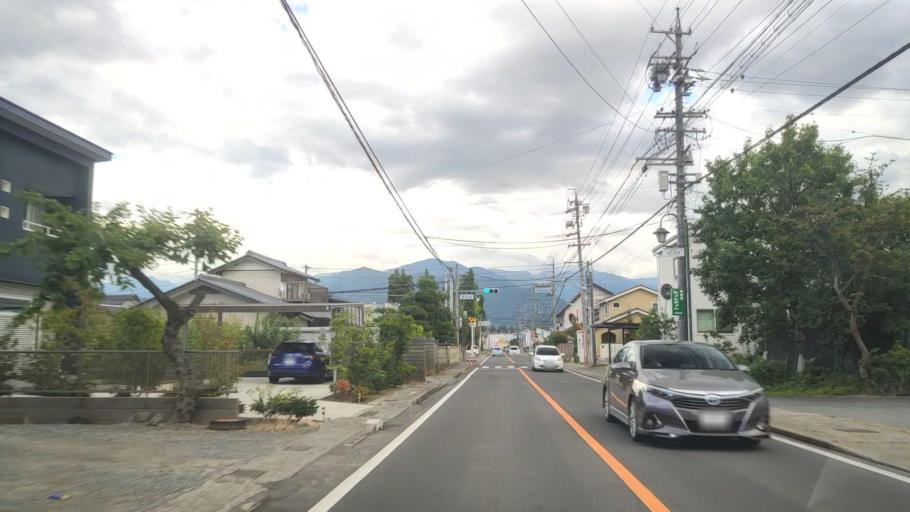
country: JP
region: Nagano
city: Suzaka
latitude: 36.6556
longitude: 138.2850
